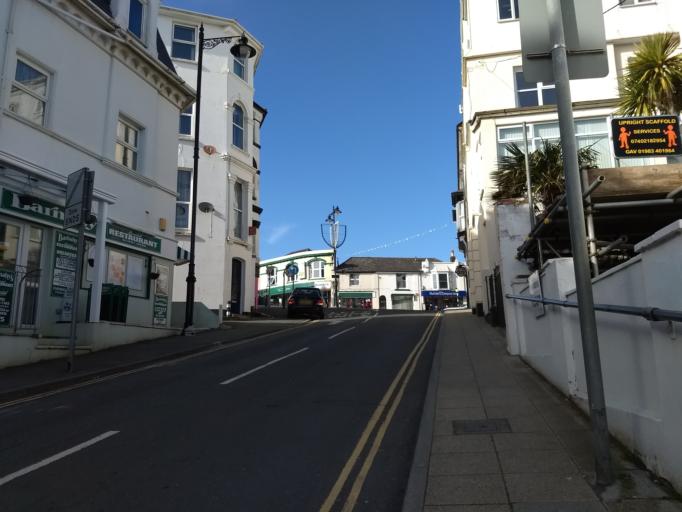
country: GB
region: England
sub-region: Isle of Wight
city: Sandown
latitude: 50.6533
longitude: -1.1556
